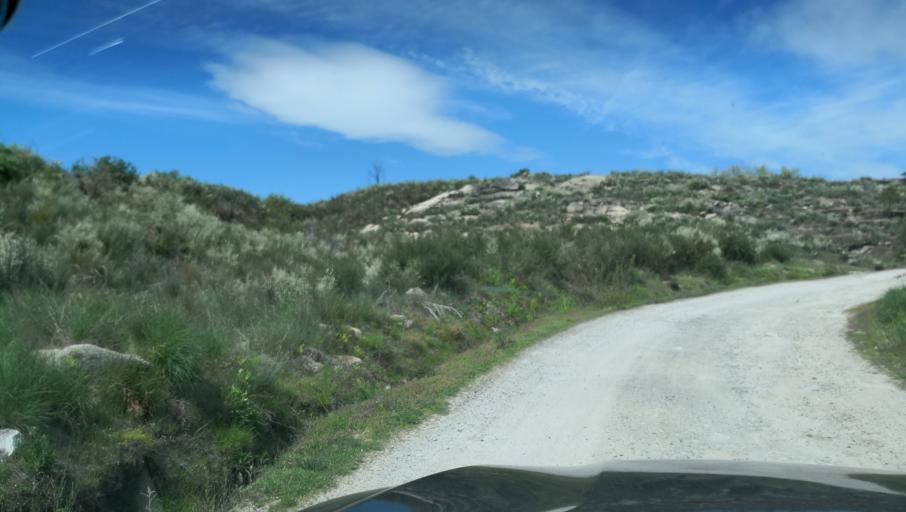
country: PT
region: Vila Real
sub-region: Vila Real
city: Vila Real
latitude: 41.3691
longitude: -7.6722
